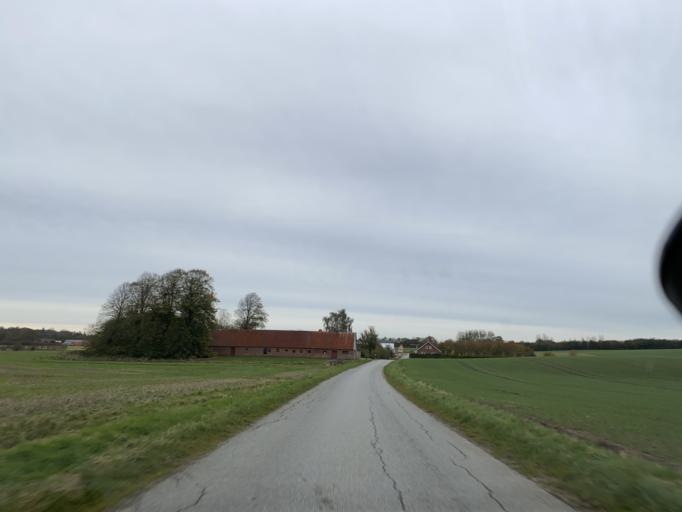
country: DK
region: Central Jutland
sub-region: Skanderborg Kommune
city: Ry
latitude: 56.1826
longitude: 9.7736
